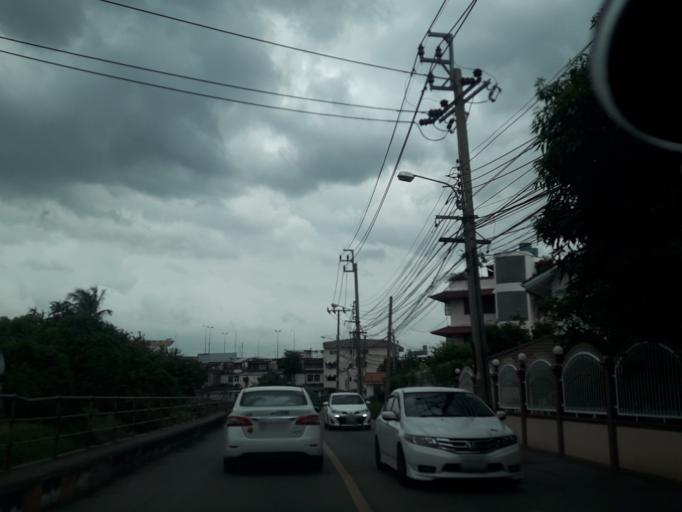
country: TH
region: Bangkok
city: Don Mueang
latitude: 13.9408
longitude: 100.6099
